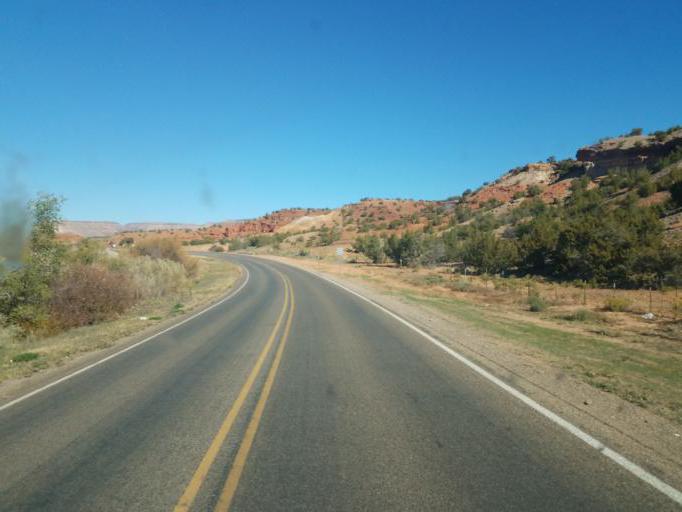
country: US
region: New Mexico
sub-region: Sandoval County
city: Jemez Pueblo
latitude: 35.6349
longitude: -106.7232
